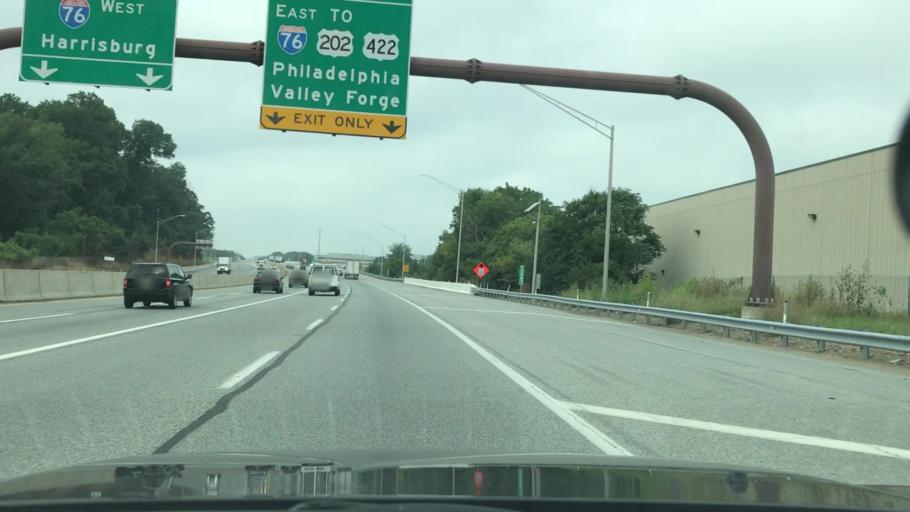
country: US
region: Pennsylvania
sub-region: Montgomery County
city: King of Prussia
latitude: 40.0935
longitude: -75.4019
